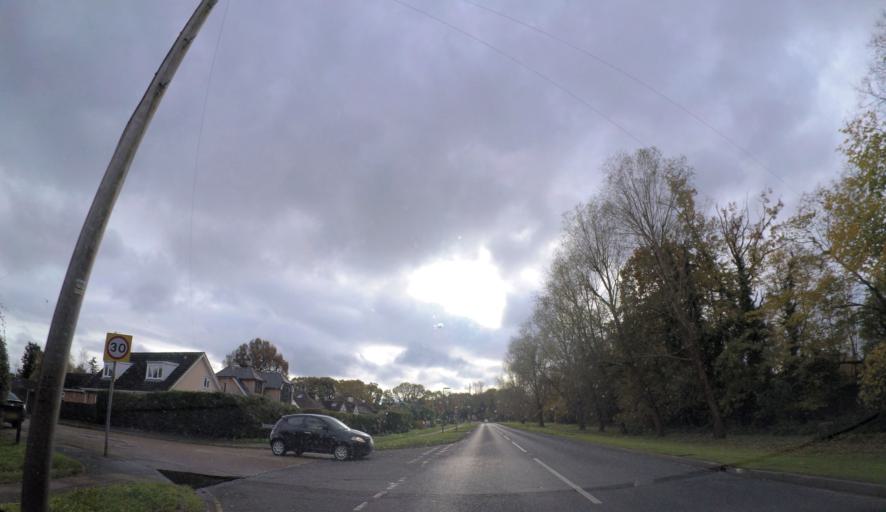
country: GB
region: England
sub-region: Surrey
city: Salfords
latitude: 51.2149
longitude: -0.1753
